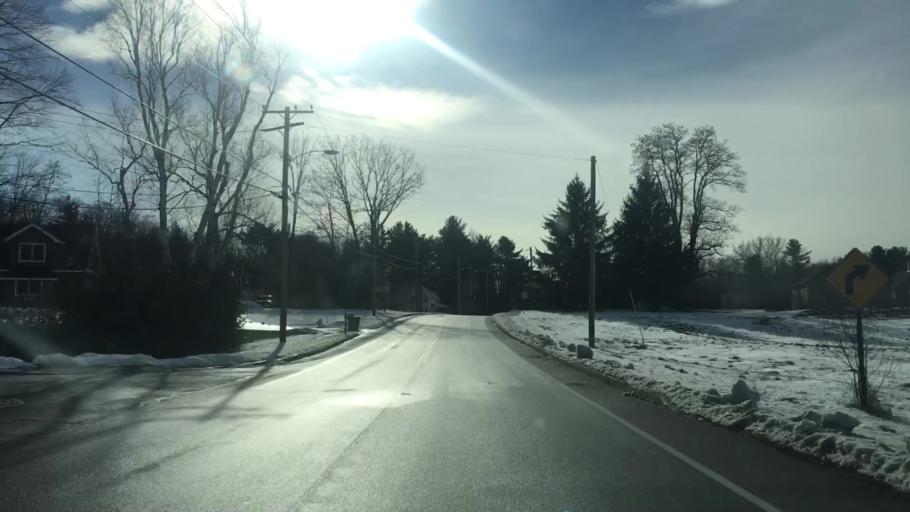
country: US
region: Maine
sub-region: York County
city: West Kennebunk
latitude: 43.4167
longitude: -70.5639
